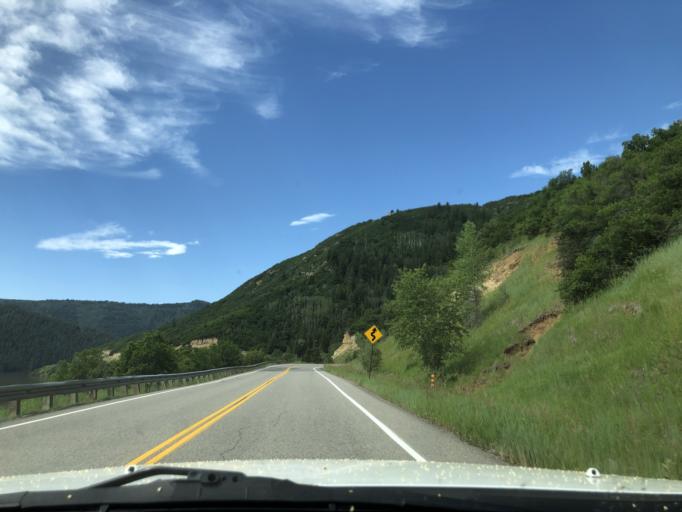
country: US
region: Colorado
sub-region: Delta County
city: Paonia
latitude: 38.9592
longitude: -107.3397
